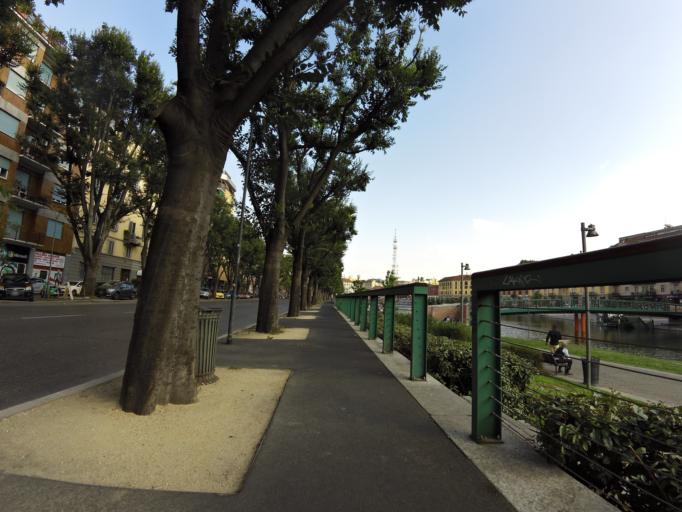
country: IT
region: Lombardy
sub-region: Citta metropolitana di Milano
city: Milano
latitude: 45.4549
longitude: 9.1747
